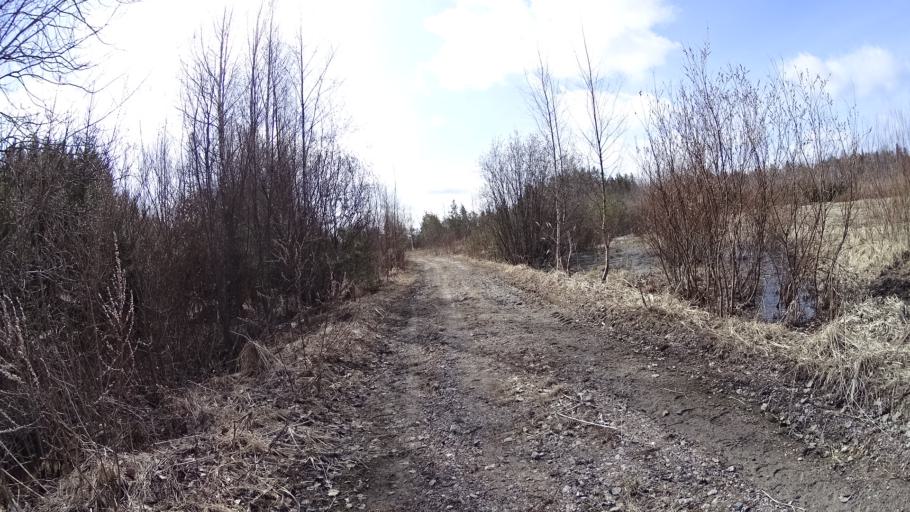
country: FI
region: Uusimaa
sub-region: Helsinki
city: Kilo
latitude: 60.3230
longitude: 24.8225
